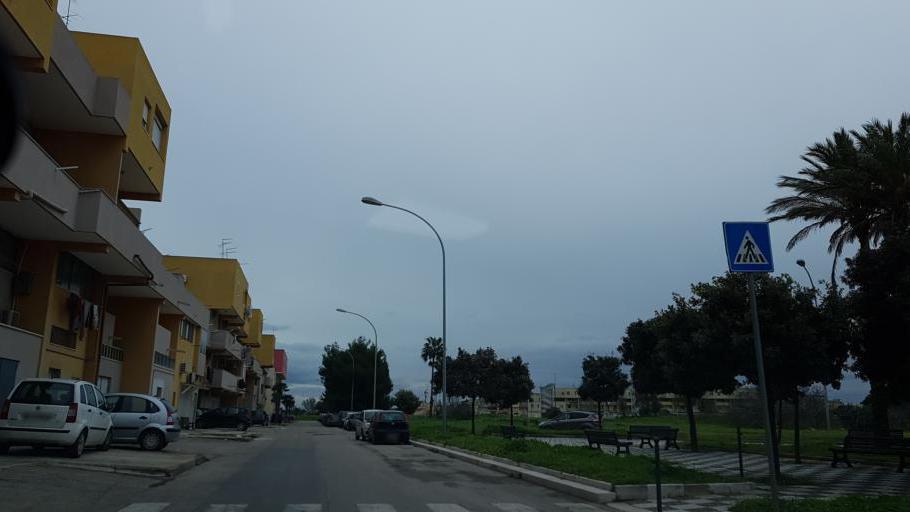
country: IT
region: Apulia
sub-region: Provincia di Brindisi
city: Brindisi
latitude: 40.6303
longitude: 17.9530
